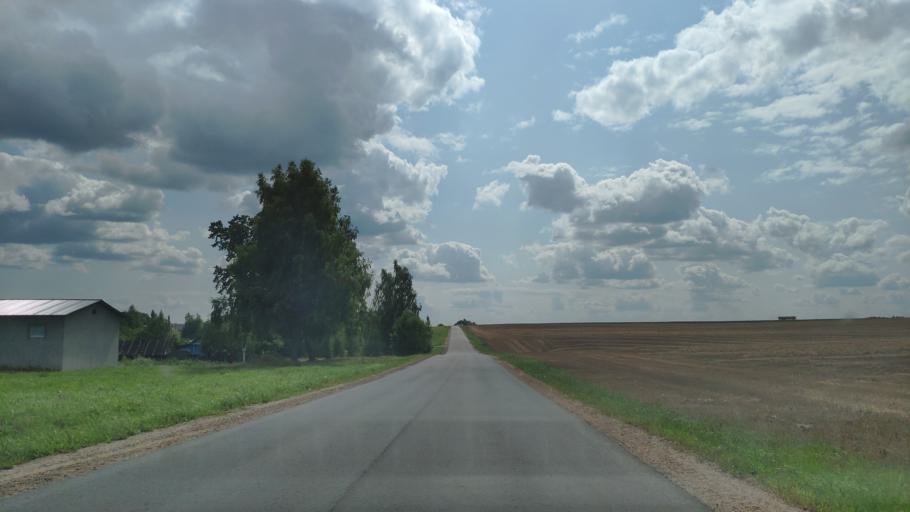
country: BY
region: Minsk
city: Khatsyezhyna
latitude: 53.8383
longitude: 27.3094
